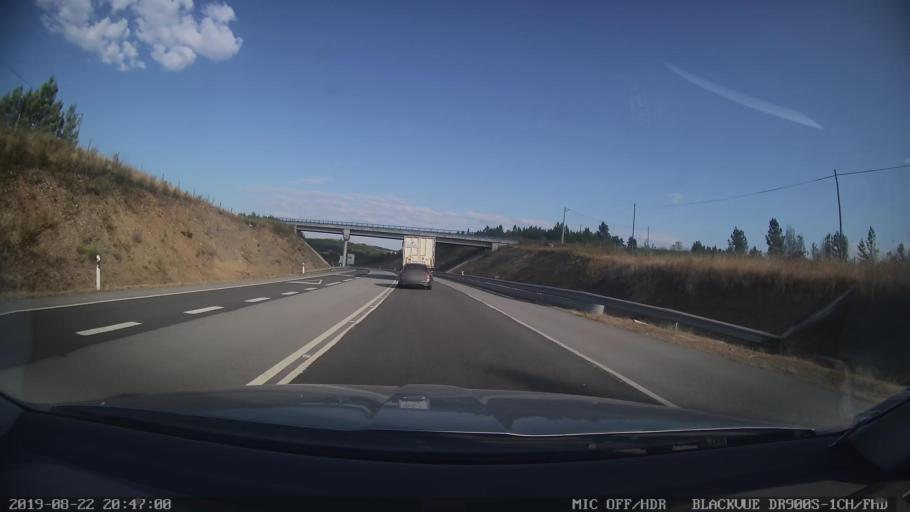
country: PT
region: Castelo Branco
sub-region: Proenca-A-Nova
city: Proenca-a-Nova
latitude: 39.7315
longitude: -7.8822
